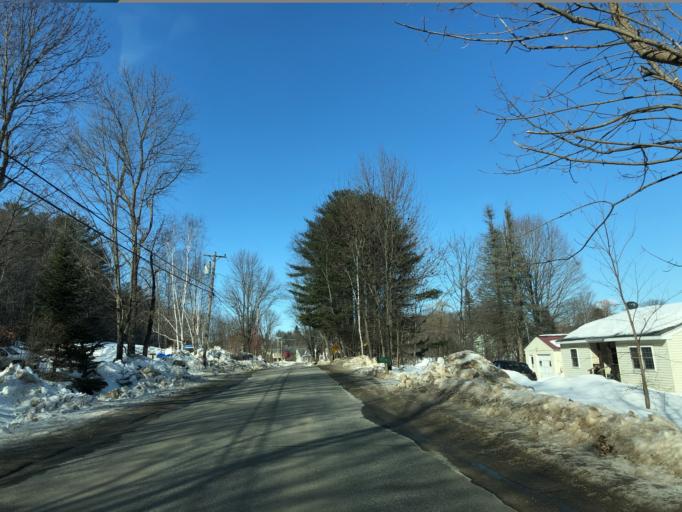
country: US
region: Maine
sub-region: Oxford County
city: Buckfield
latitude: 44.2840
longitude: -70.3588
